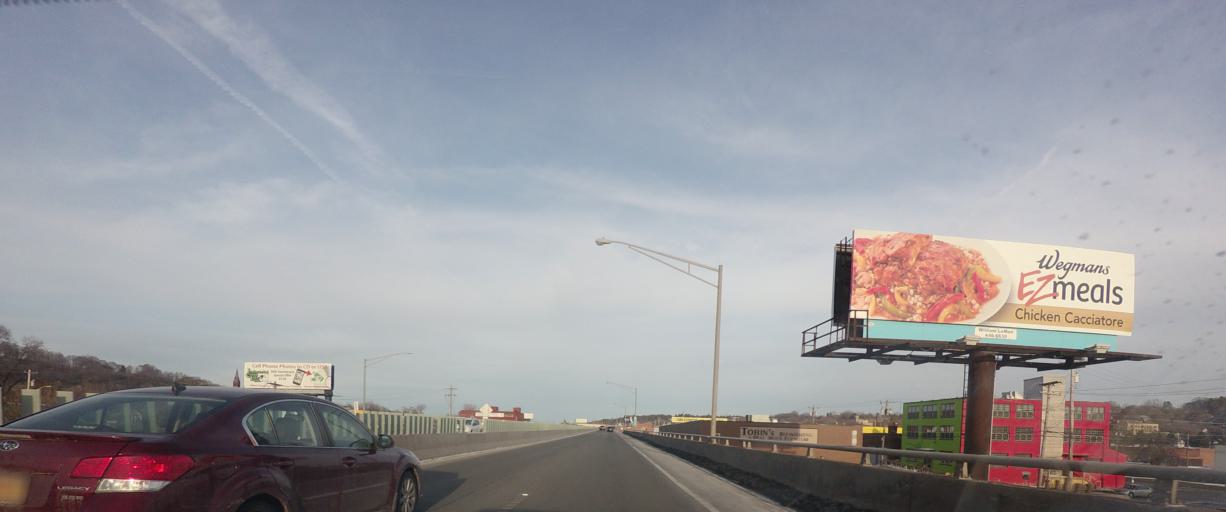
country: US
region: New York
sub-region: Onondaga County
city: Syracuse
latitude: 43.0513
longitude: -76.1324
